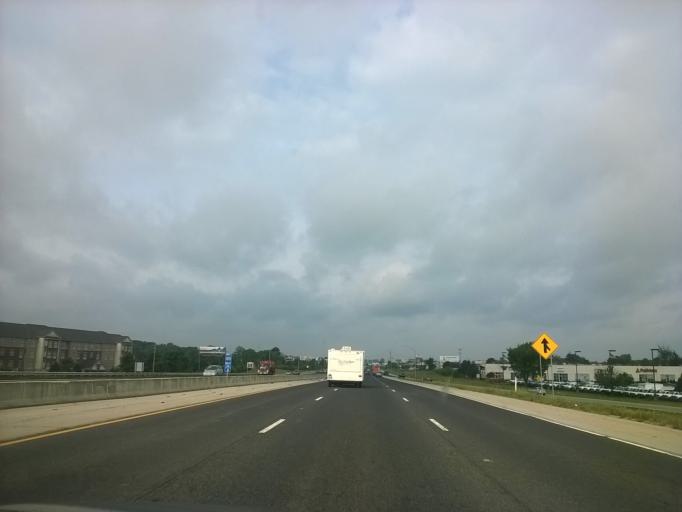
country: US
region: Indiana
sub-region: Boone County
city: Zionsville
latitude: 39.9238
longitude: -86.2294
